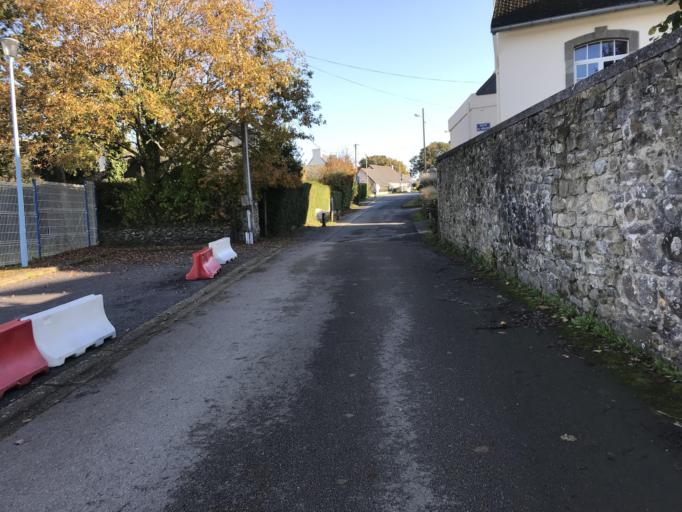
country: FR
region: Brittany
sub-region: Departement du Finistere
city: Hopital-Camfrout
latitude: 48.3268
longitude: -4.2397
